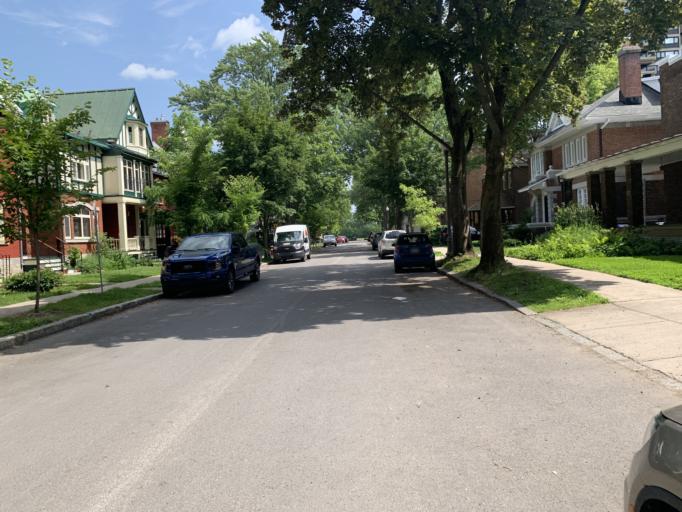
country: CA
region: Quebec
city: Quebec
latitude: 46.8008
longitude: -71.2294
